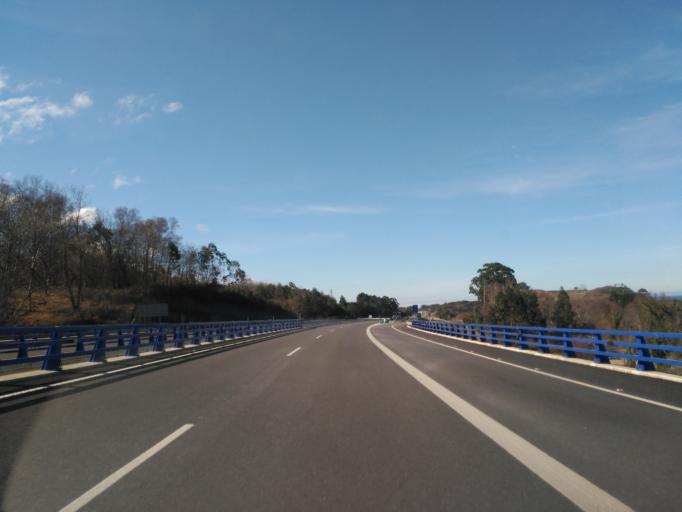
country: ES
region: Asturias
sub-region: Province of Asturias
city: Llanes
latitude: 43.3942
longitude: -4.6485
